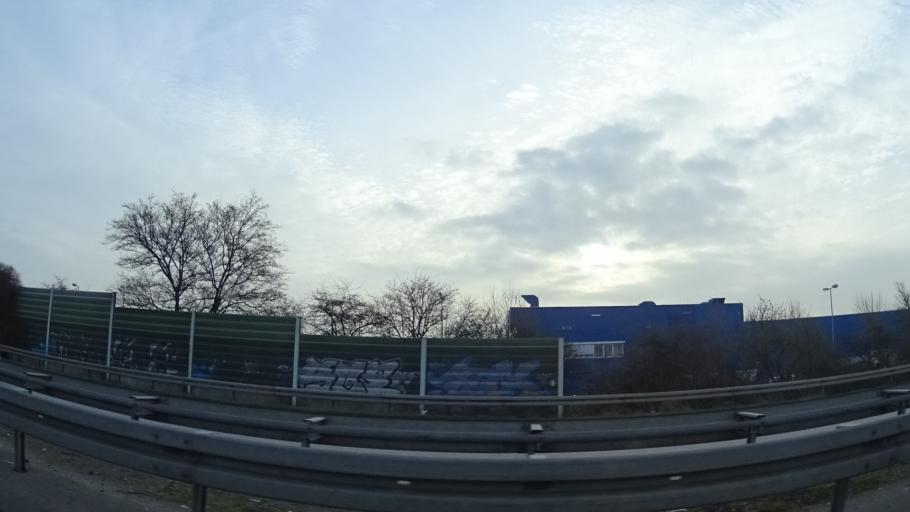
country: DE
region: Baden-Wuerttemberg
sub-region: Karlsruhe Region
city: Walldorf
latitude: 49.3065
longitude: 8.6278
